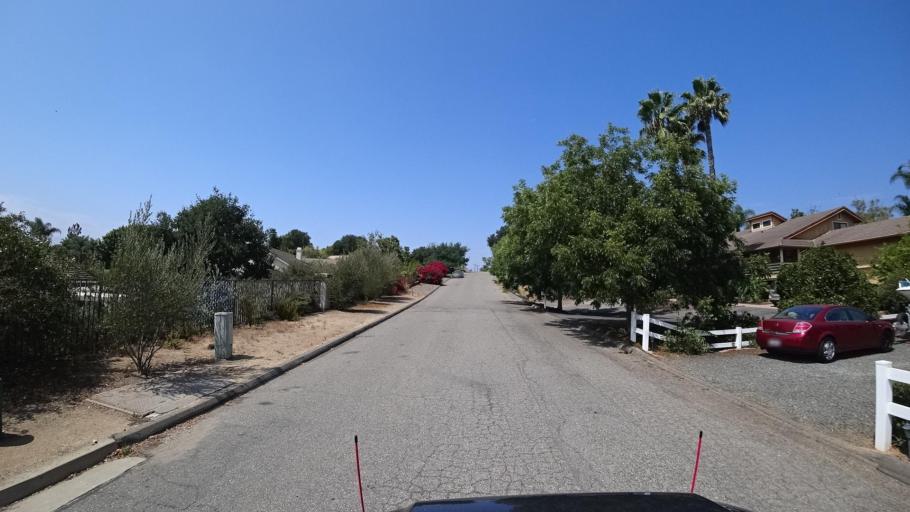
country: US
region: California
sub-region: San Diego County
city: Fallbrook
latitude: 33.3583
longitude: -117.2325
